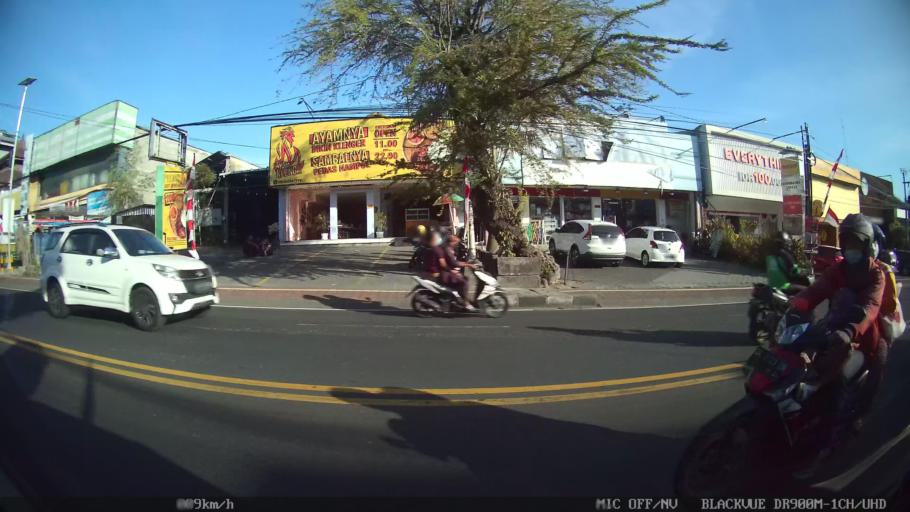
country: ID
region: Bali
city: Banjar Kertasari
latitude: -8.6364
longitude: 115.2149
